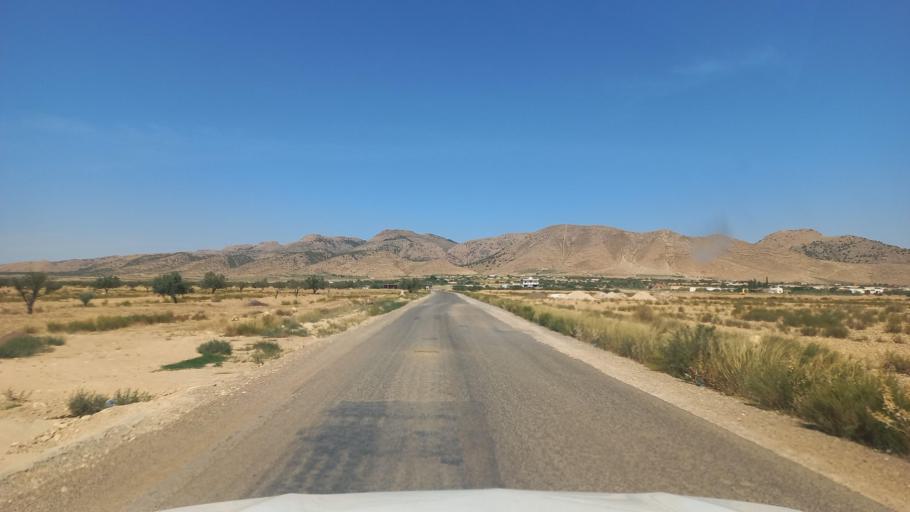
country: TN
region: Al Qasrayn
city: Sbiba
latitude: 35.4389
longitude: 9.0775
